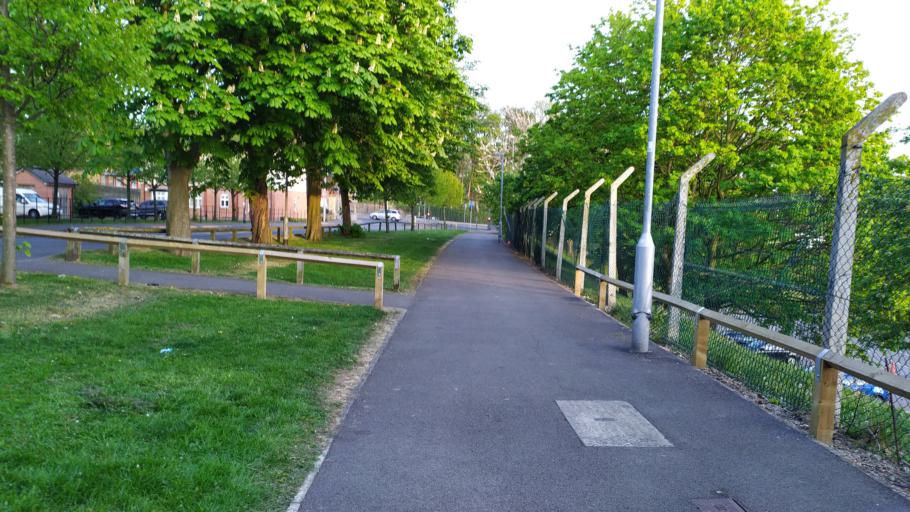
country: GB
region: England
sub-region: City and Borough of Leeds
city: Shadwell
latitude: 53.8070
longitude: -1.4756
